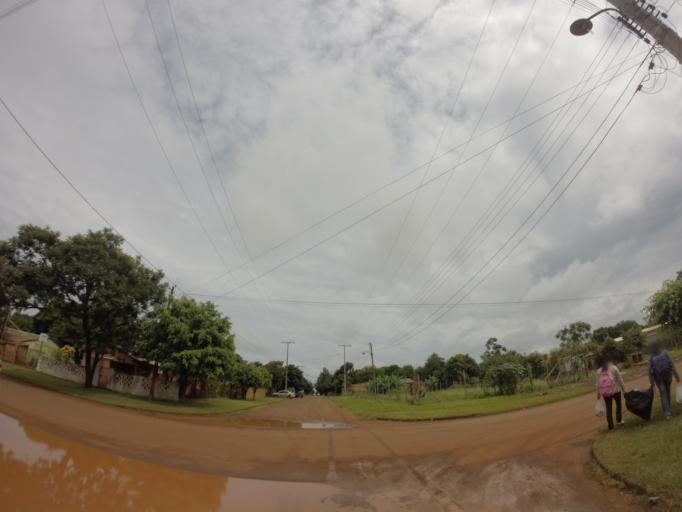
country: PY
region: Alto Parana
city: Ciudad del Este
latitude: -25.3855
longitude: -54.6530
